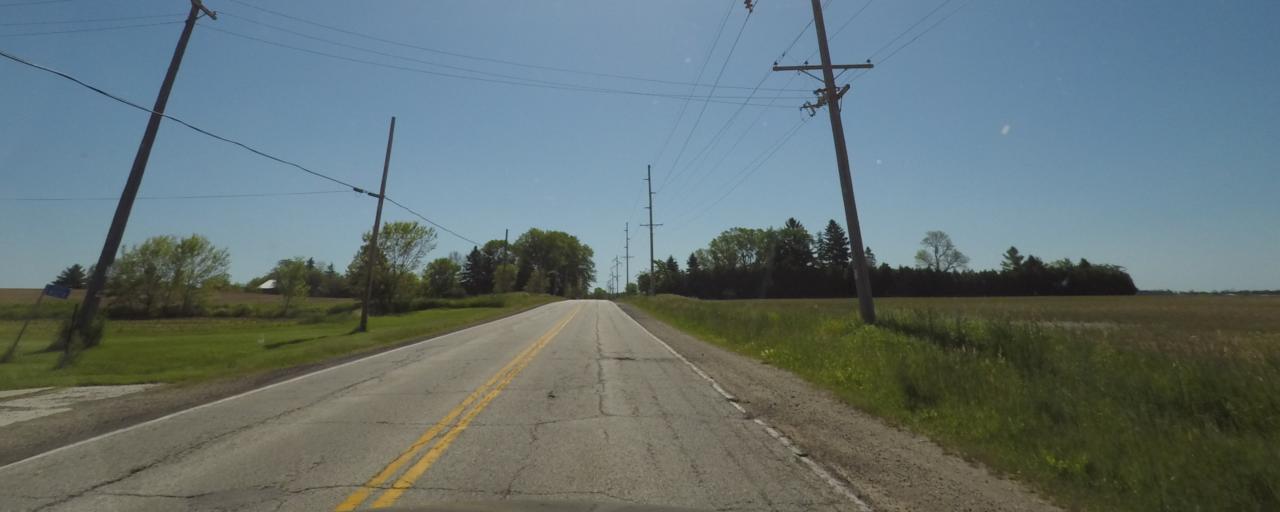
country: US
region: Wisconsin
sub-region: Sheboygan County
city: Sheboygan Falls
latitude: 43.7414
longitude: -87.8592
